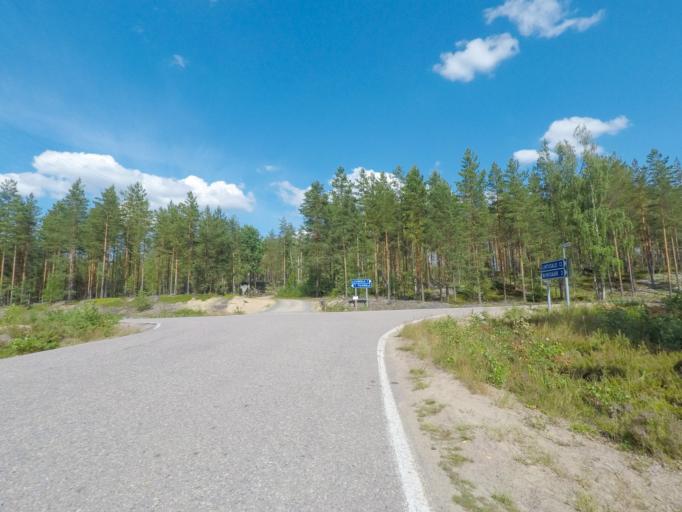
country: FI
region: Southern Savonia
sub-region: Mikkeli
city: Puumala
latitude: 61.4603
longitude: 28.1761
